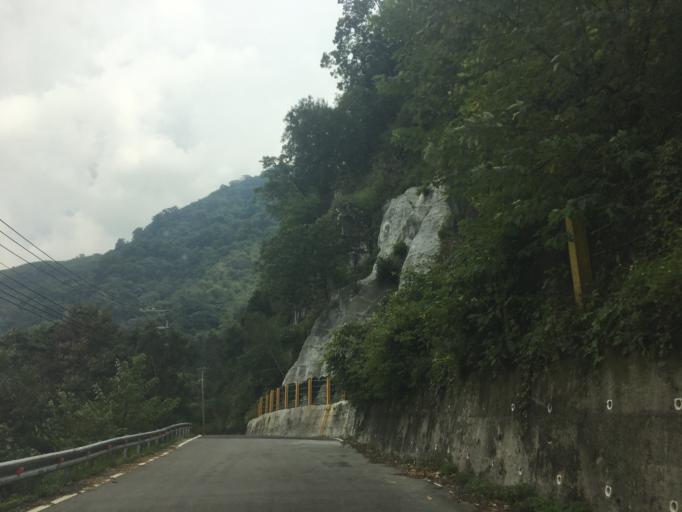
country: TW
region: Taiwan
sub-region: Miaoli
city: Miaoli
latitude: 24.3566
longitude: 120.9475
